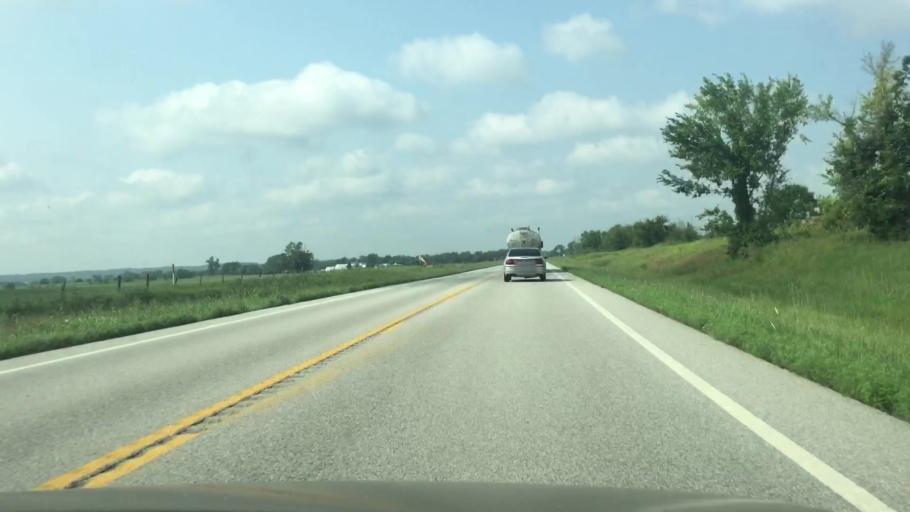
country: US
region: Kansas
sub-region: Anderson County
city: Garnett
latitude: 38.2947
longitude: -95.1952
